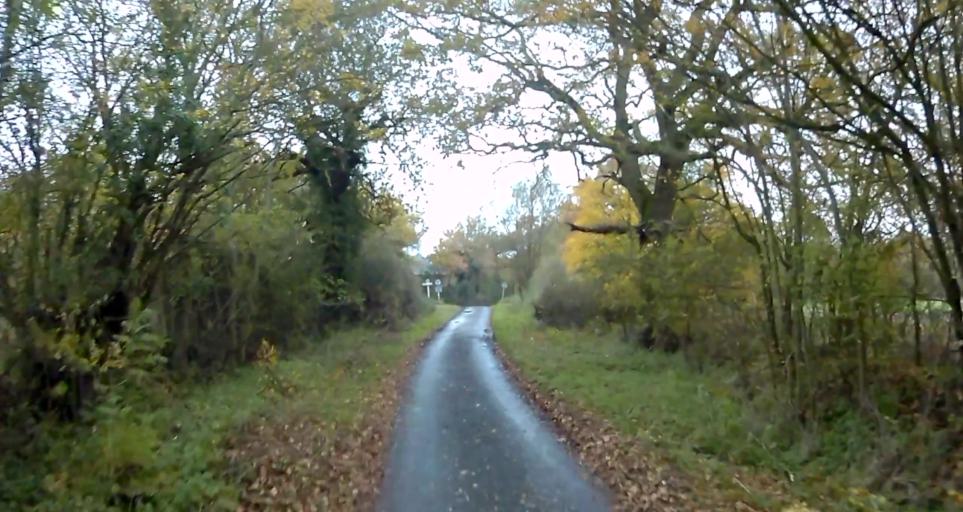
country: GB
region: England
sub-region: Hampshire
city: Odiham
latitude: 51.2459
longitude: -0.9029
